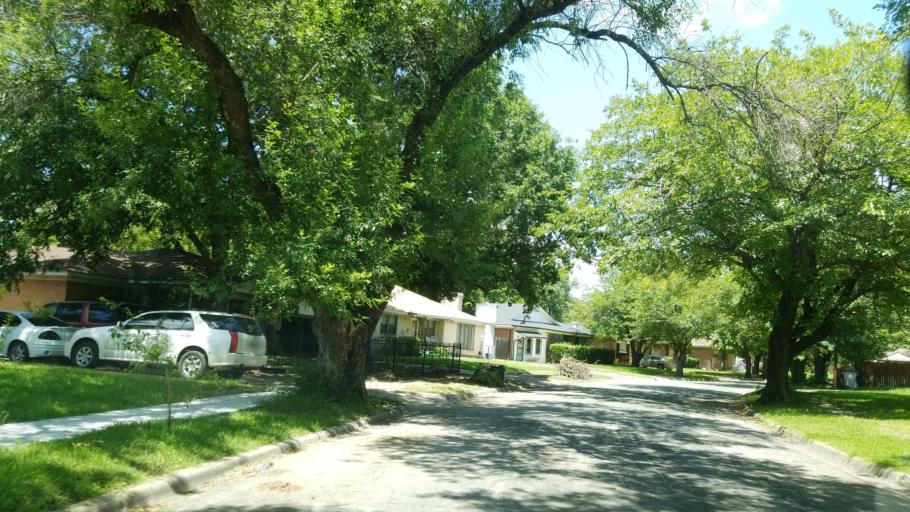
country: US
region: Texas
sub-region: Dallas County
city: Balch Springs
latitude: 32.7362
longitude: -96.7076
